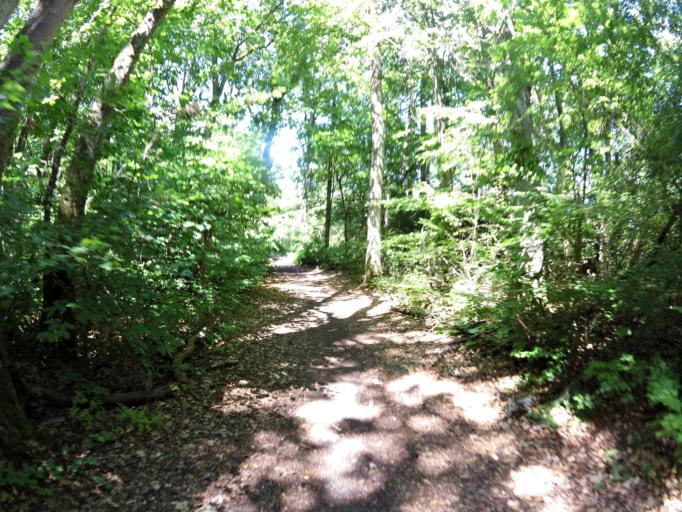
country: DE
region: Bavaria
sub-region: Regierungsbezirk Unterfranken
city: Thungersheim
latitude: 49.8943
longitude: 9.8501
